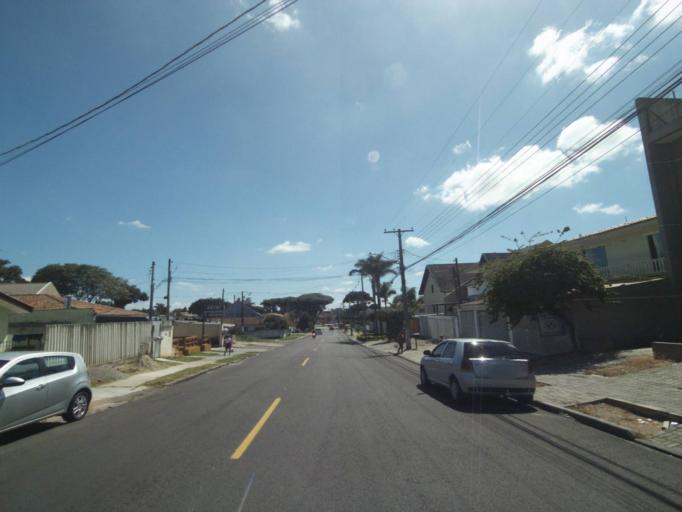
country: BR
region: Parana
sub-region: Pinhais
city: Pinhais
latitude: -25.4367
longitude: -49.2228
